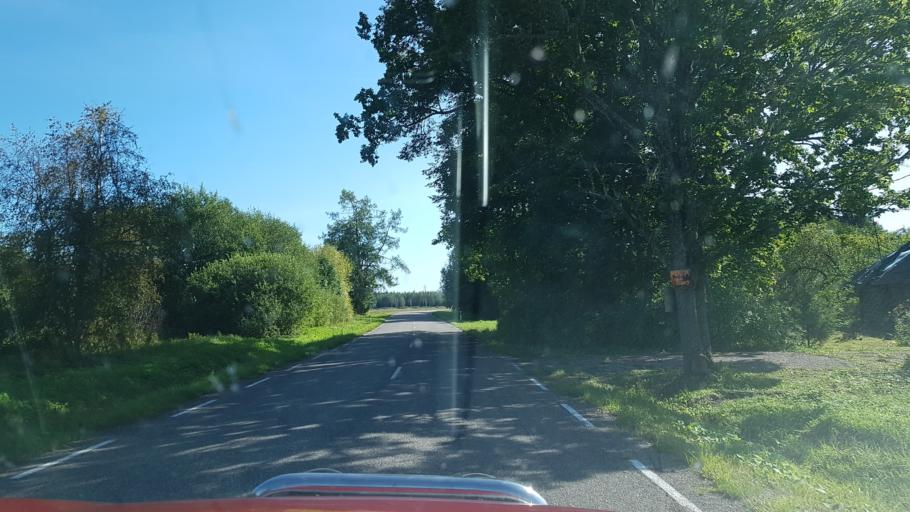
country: EE
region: Paernumaa
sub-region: Saarde vald
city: Kilingi-Nomme
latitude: 58.0310
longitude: 25.0097
